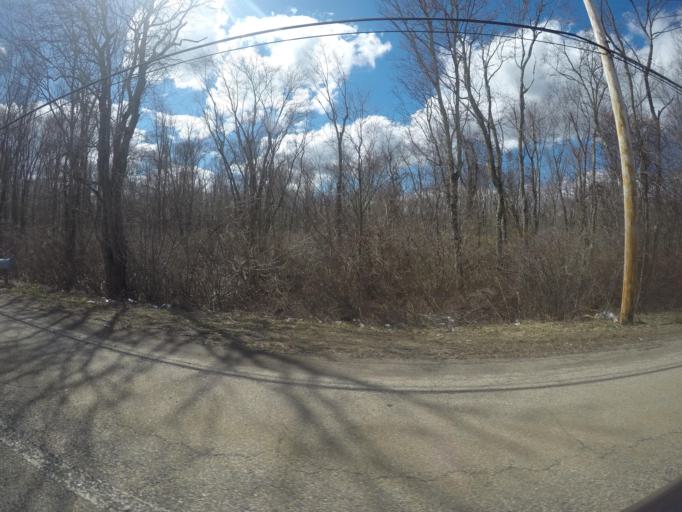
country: US
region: Massachusetts
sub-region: Bristol County
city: Raynham
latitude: 41.9961
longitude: -71.0679
